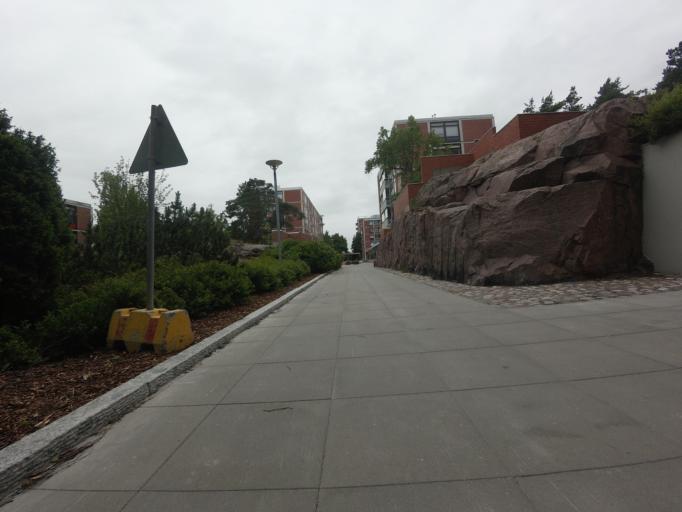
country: FI
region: Uusimaa
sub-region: Helsinki
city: Koukkuniemi
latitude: 60.1757
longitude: 24.7357
